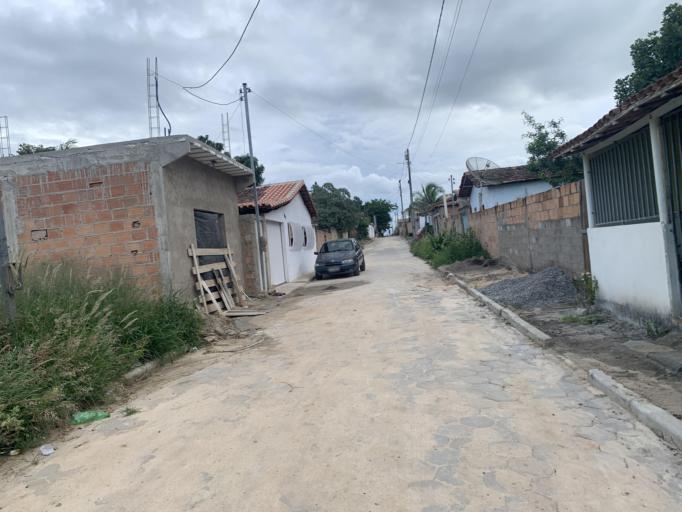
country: BR
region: Bahia
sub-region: Medeiros Neto
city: Medeiros Neto
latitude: -17.3900
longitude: -40.2324
